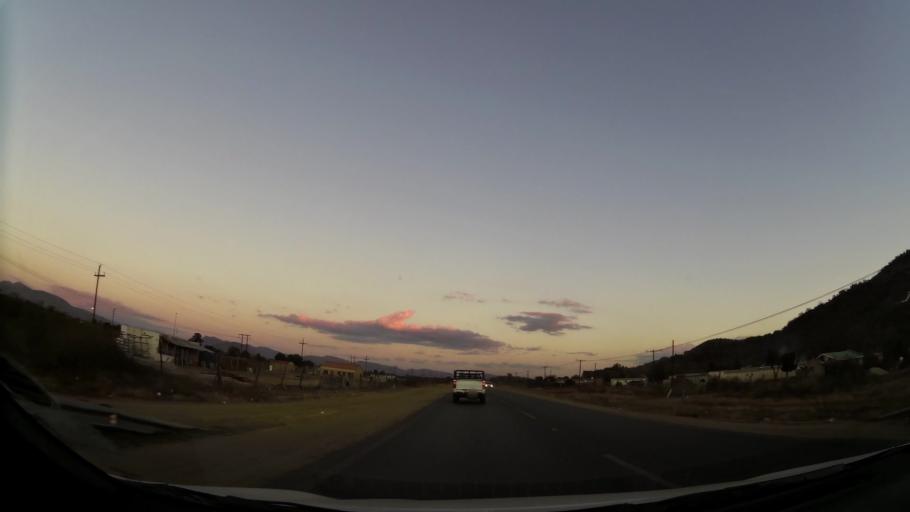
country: ZA
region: Limpopo
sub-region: Waterberg District Municipality
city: Mokopane
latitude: -24.1444
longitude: 28.9697
